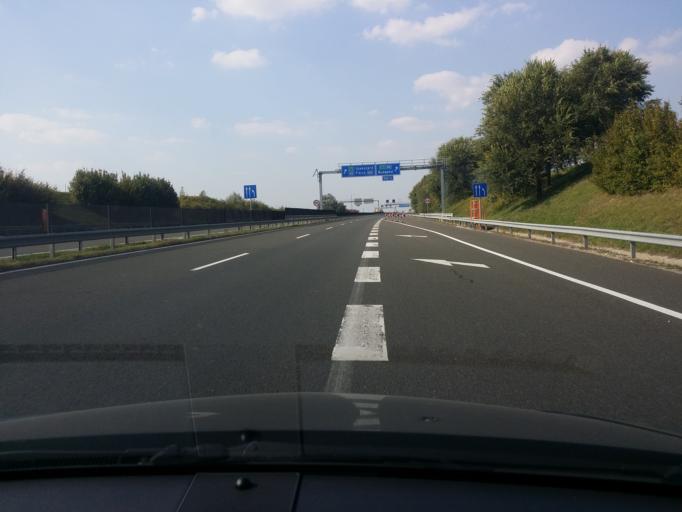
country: HU
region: Fejer
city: Baracs
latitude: 46.9140
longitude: 18.9141
